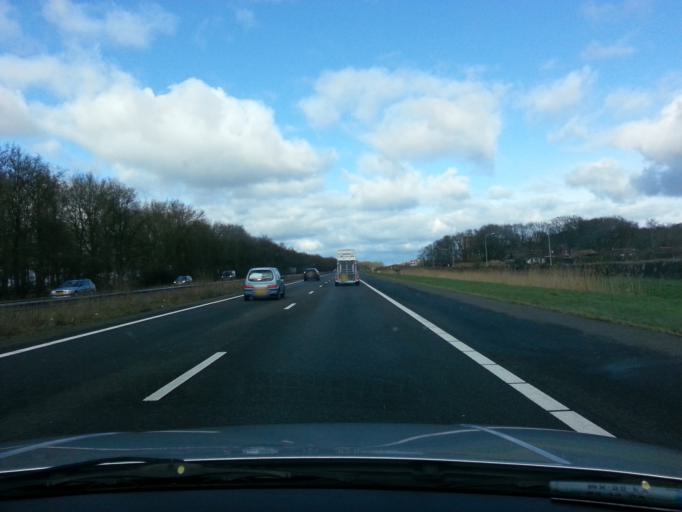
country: NL
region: Gelderland
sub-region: Gemeente Ermelo
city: Horst
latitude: 52.3201
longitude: 5.5713
